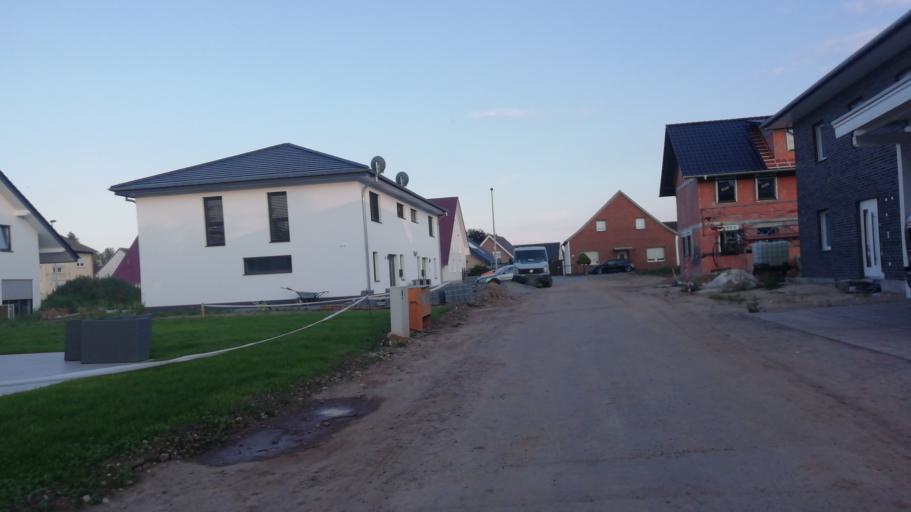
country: DE
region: North Rhine-Westphalia
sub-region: Regierungsbezirk Detmold
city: Minden
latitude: 52.2698
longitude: 8.8987
